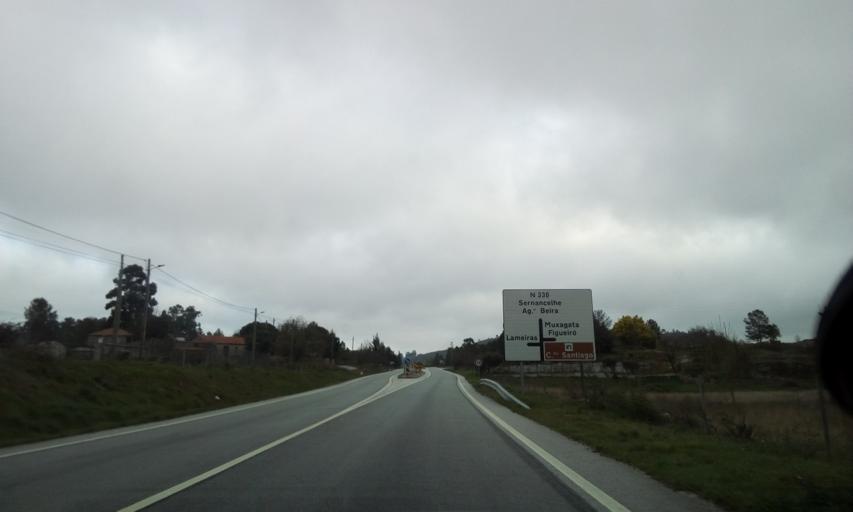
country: PT
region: Guarda
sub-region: Fornos de Algodres
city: Fornos de Algodres
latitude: 40.6355
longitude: -7.4989
